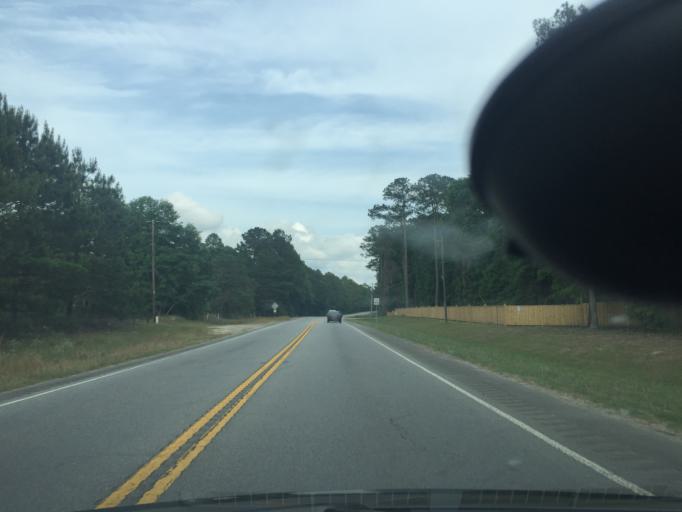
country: US
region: Georgia
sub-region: Bryan County
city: Richmond Hill
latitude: 32.0167
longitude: -81.3075
